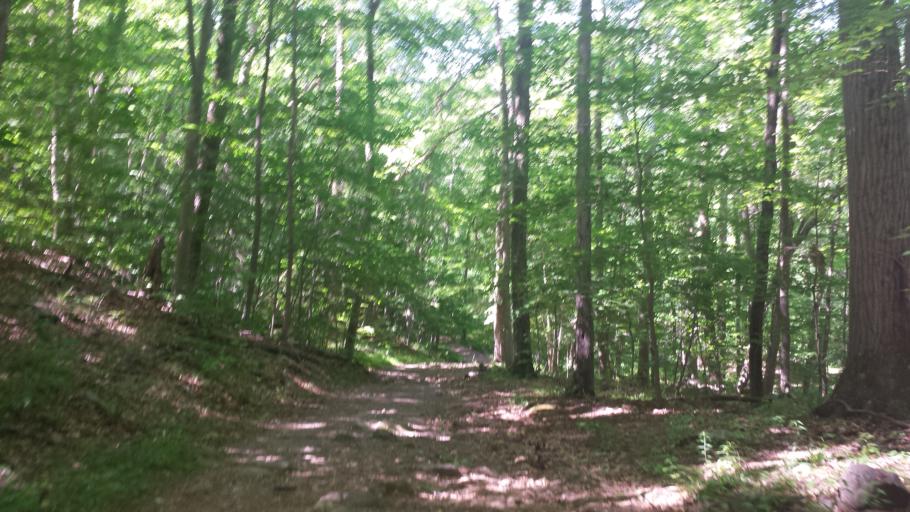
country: US
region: New York
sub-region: Westchester County
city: Pound Ridge
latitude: 41.2413
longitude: -73.5969
